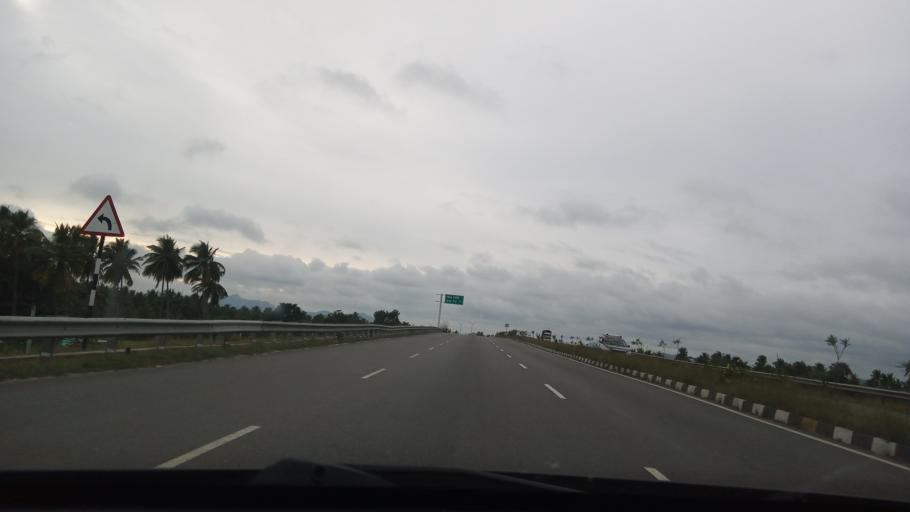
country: IN
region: Tamil Nadu
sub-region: Vellore
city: Vaniyambadi
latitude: 12.6549
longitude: 78.5920
